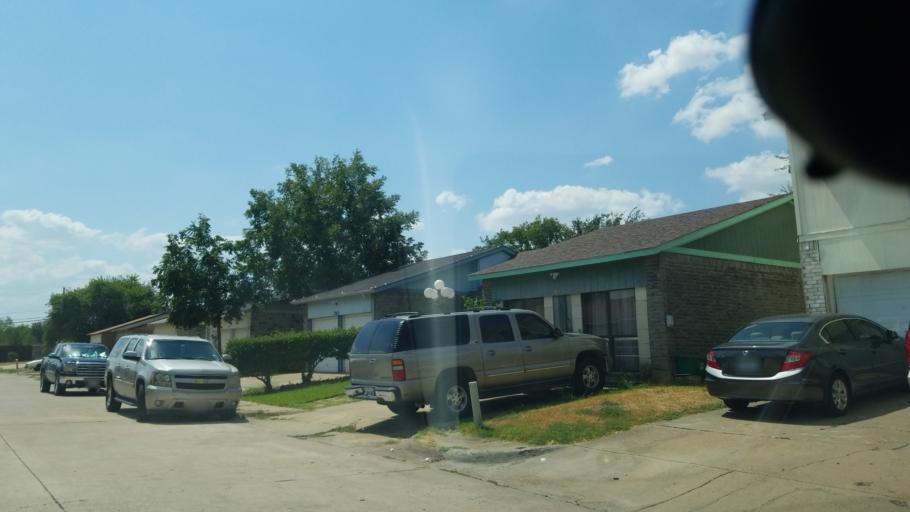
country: US
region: Texas
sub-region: Dallas County
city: Grand Prairie
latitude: 32.7000
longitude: -96.9894
